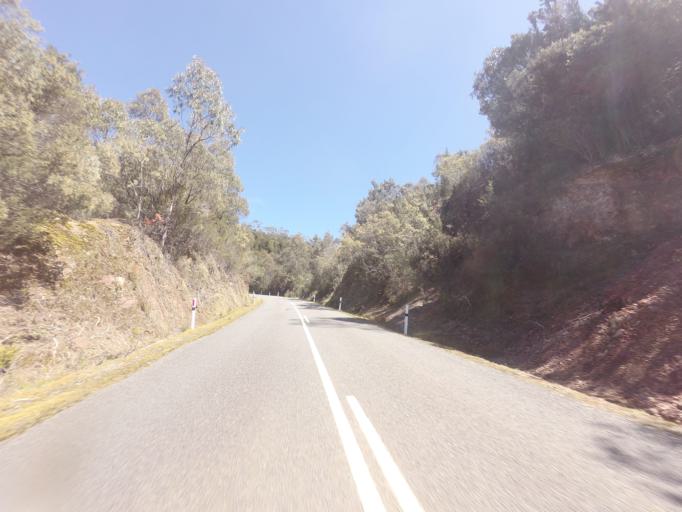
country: AU
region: Tasmania
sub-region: Huon Valley
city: Geeveston
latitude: -42.8139
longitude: 146.3701
